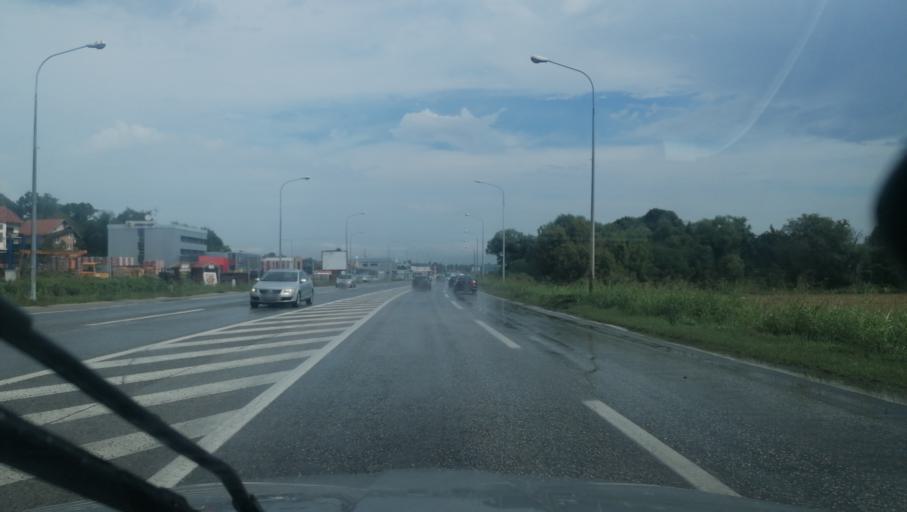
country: BA
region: Republika Srpska
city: Banja Luka
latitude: 44.8118
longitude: 17.1990
